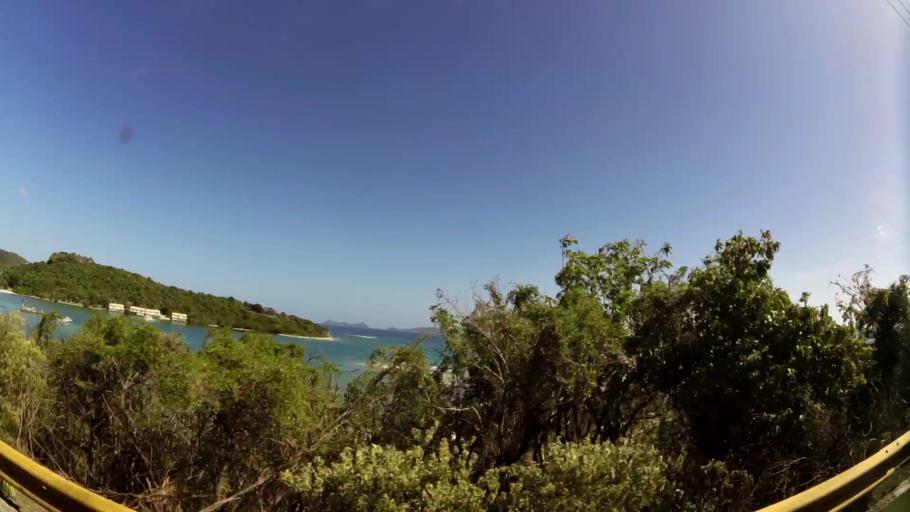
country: VG
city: Tortola
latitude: 18.4138
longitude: -64.5879
